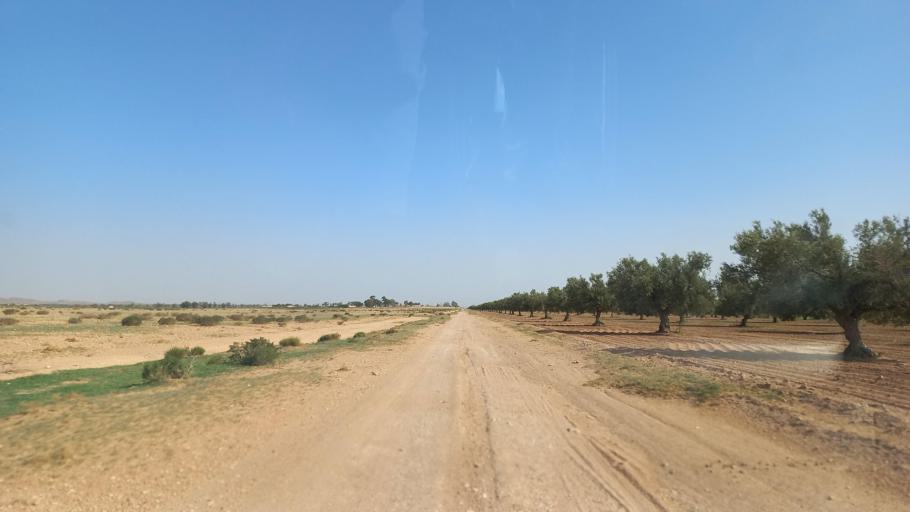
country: TN
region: Al Qasrayn
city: Kasserine
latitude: 35.3048
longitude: 9.0238
